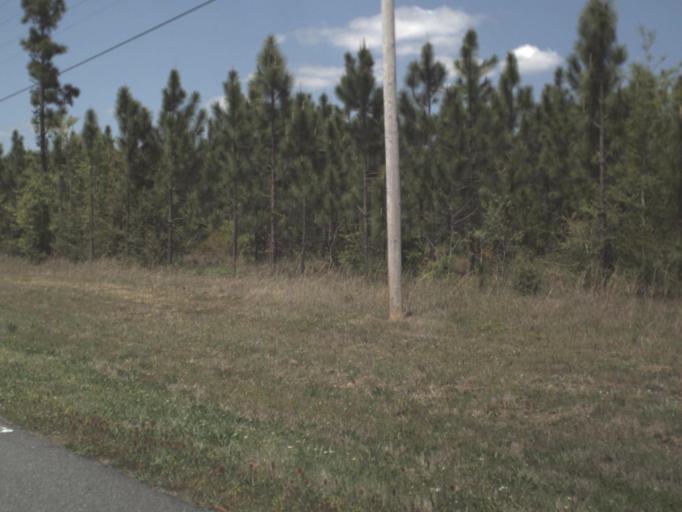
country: US
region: Alabama
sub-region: Escambia County
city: East Brewton
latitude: 30.9454
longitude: -87.0325
